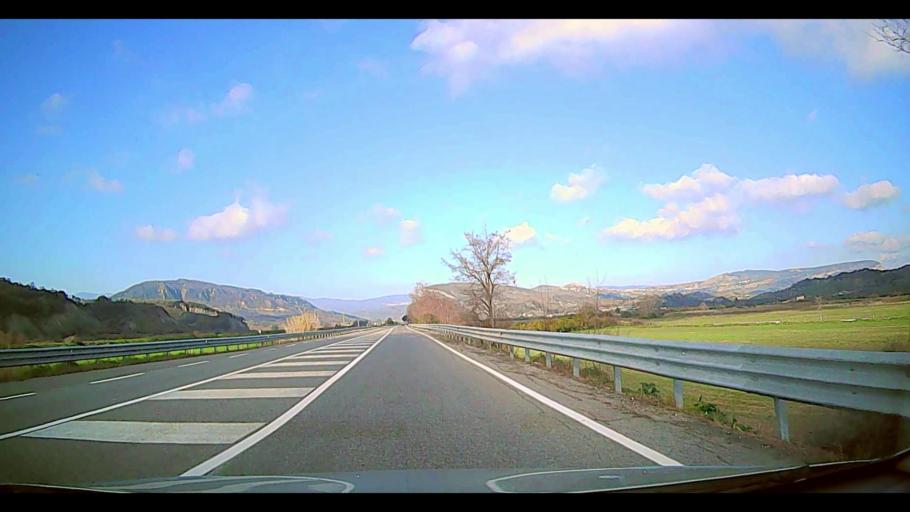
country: IT
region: Calabria
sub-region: Provincia di Crotone
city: Santa Severina
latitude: 39.1759
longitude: 16.9315
